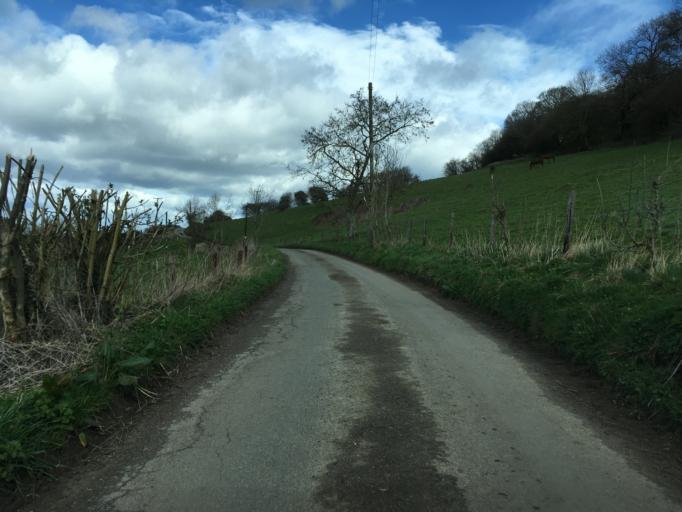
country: GB
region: England
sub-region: South Gloucestershire
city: Horton
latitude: 51.5673
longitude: -2.3379
